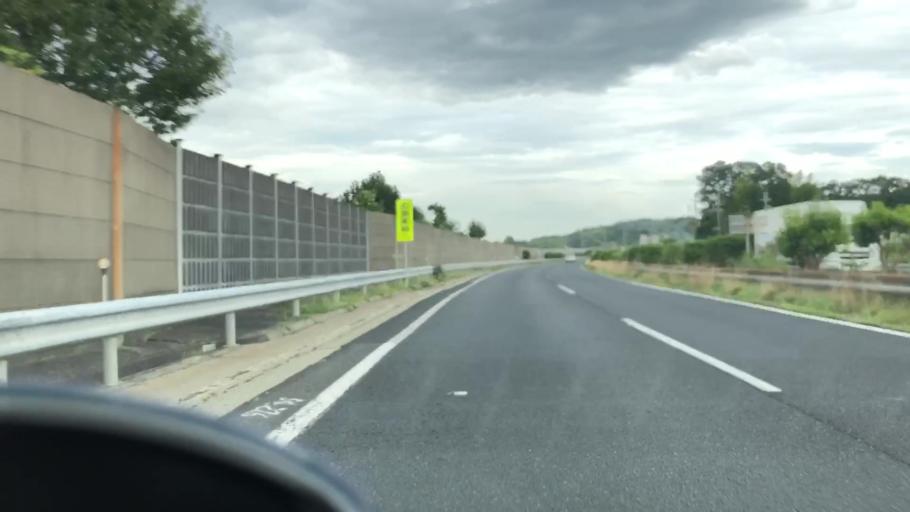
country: JP
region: Hyogo
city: Yashiro
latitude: 34.9179
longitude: 135.0177
